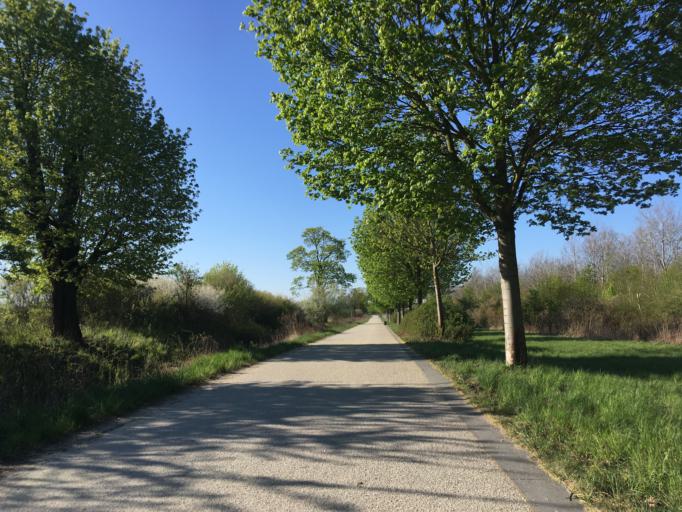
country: DE
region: Berlin
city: Wartenberg
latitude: 52.5859
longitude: 13.5042
